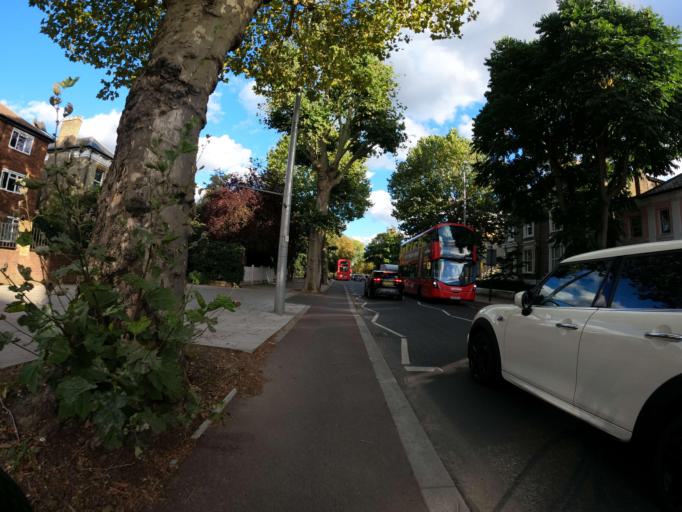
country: GB
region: England
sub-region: Greater London
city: Ealing Broadway
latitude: 51.5136
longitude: -0.2983
